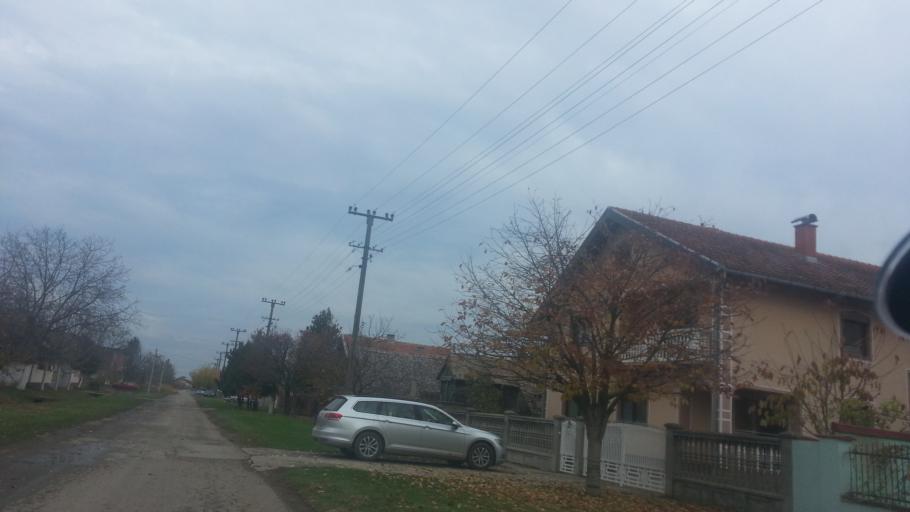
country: RS
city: Golubinci
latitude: 44.9868
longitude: 20.0714
